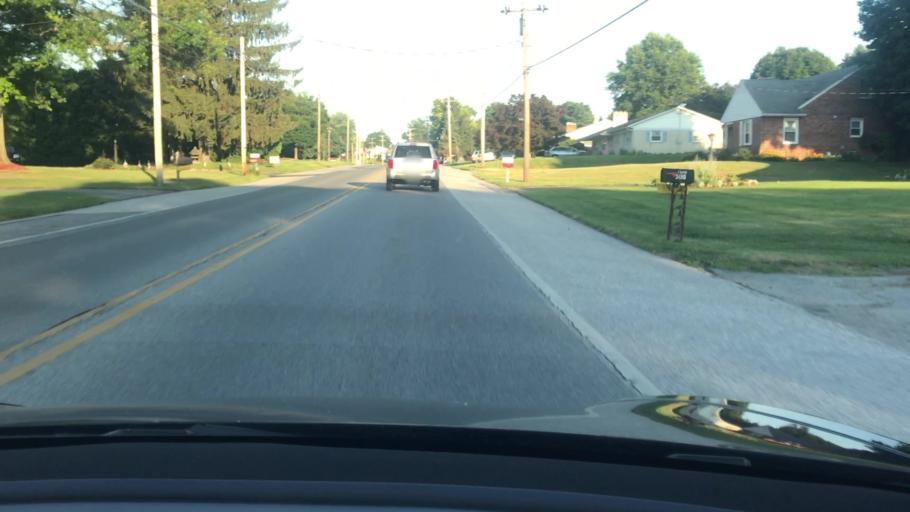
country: US
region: Pennsylvania
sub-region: York County
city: Weigelstown
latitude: 39.9868
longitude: -76.8314
